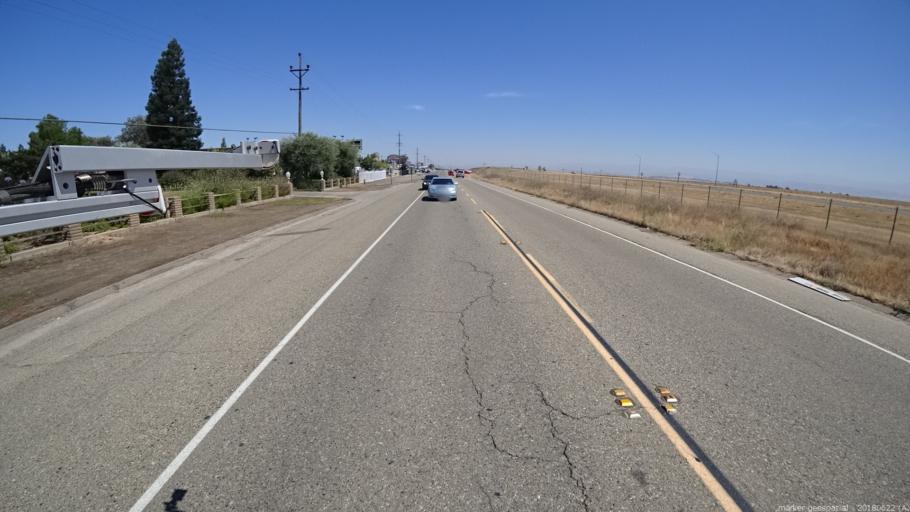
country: US
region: California
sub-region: Madera County
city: Bonadelle Ranchos-Madera Ranchos
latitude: 36.9042
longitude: -119.7934
